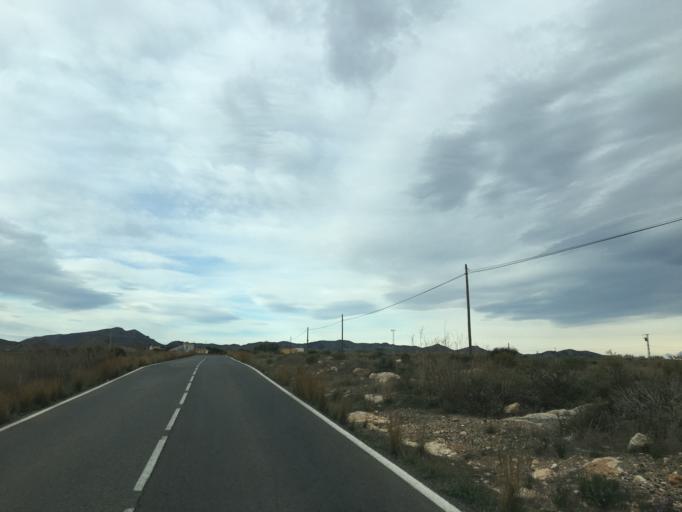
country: ES
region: Murcia
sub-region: Murcia
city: Fuente-Alamo de Murcia
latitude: 37.6194
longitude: -1.0783
